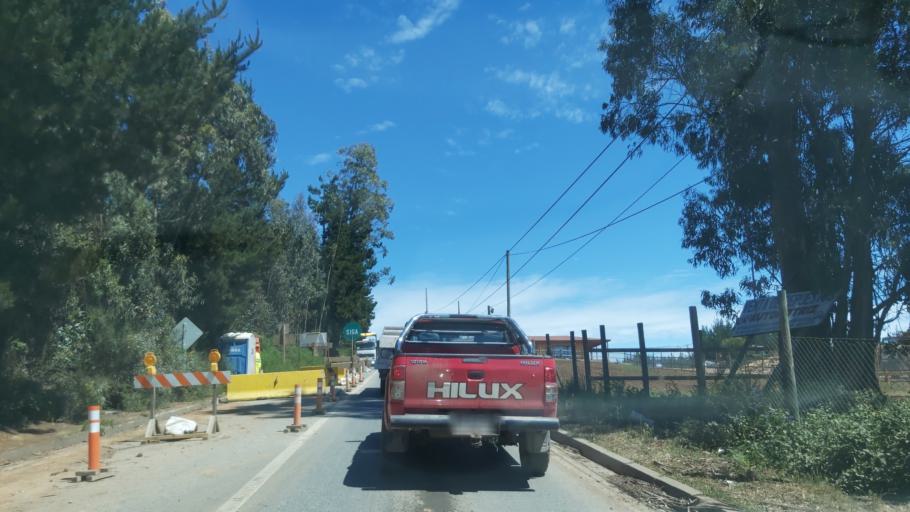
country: CL
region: Maule
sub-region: Provincia de Talca
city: Constitucion
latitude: -35.3881
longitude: -72.4240
